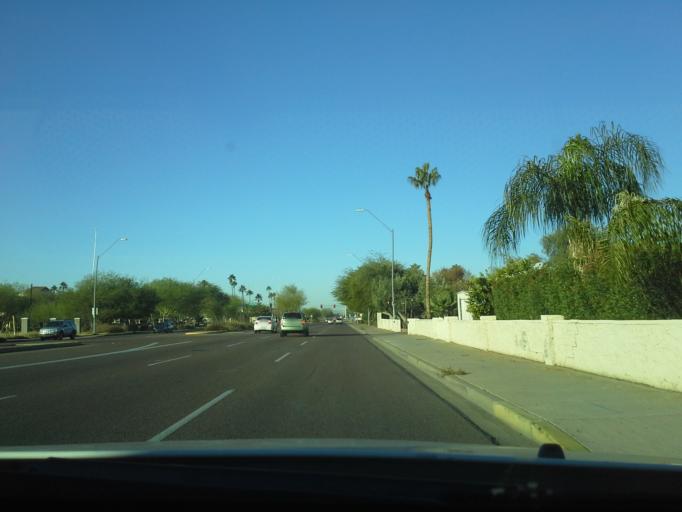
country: US
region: Arizona
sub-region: Maricopa County
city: Paradise Valley
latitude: 33.6405
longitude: -112.0544
